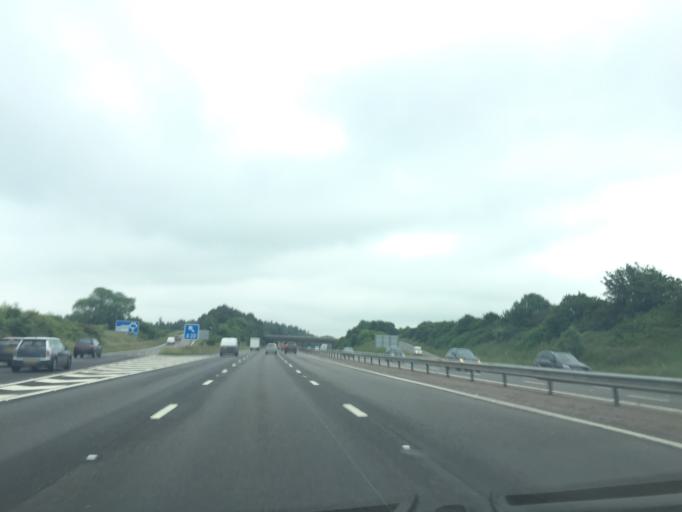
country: GB
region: England
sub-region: Hampshire
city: Basingstoke
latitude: 51.2170
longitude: -1.1635
